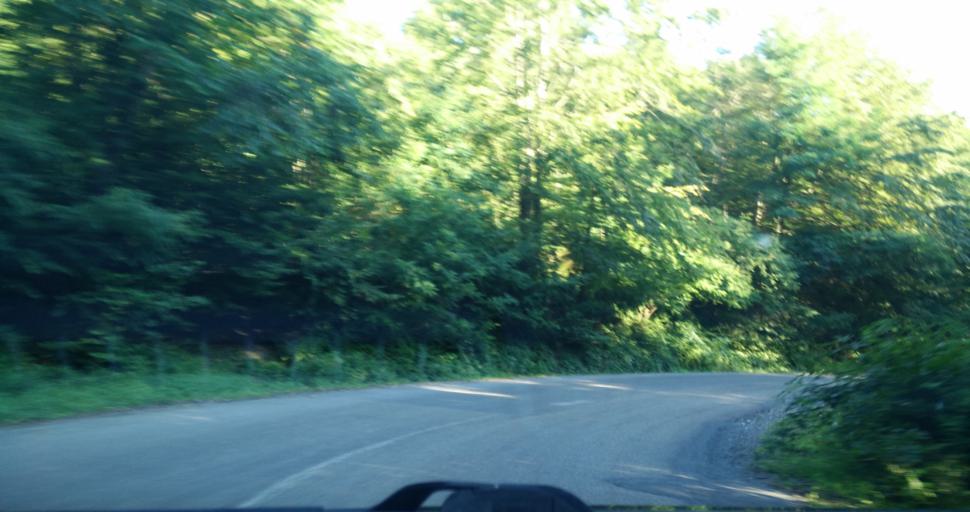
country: RO
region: Bihor
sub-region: Oras Nucet
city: Nucet
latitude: 46.4911
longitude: 22.6074
